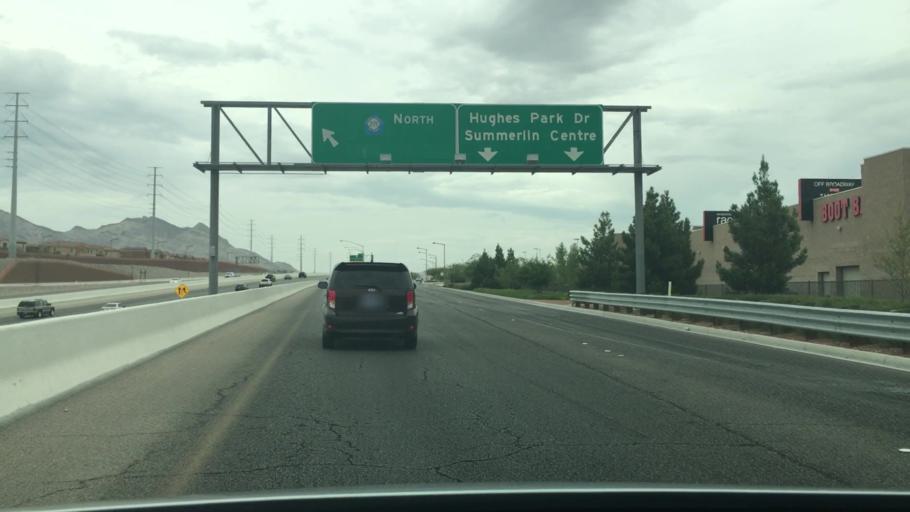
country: US
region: Nevada
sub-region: Clark County
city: Summerlin South
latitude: 36.1461
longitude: -115.3362
